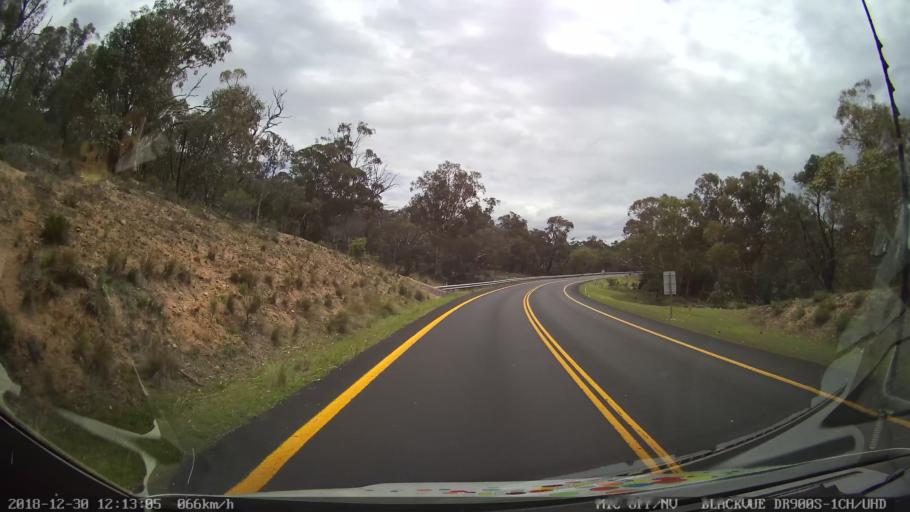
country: AU
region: New South Wales
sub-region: Snowy River
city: Jindabyne
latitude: -36.3518
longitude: 148.5857
